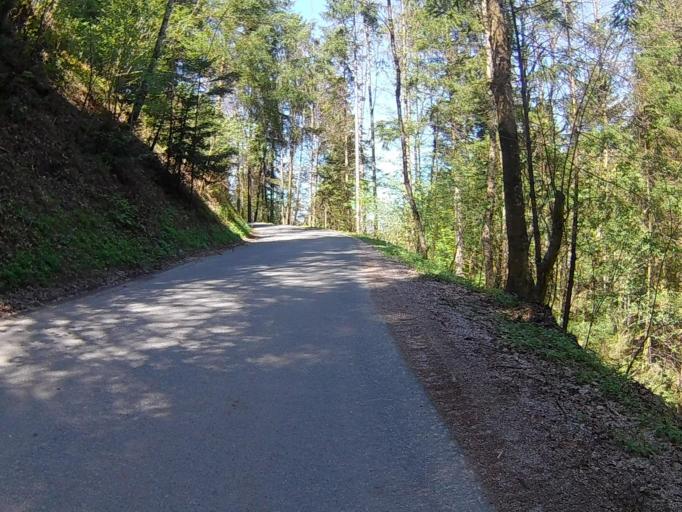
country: SI
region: Ruse
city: Ruse
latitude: 46.5300
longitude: 15.5127
